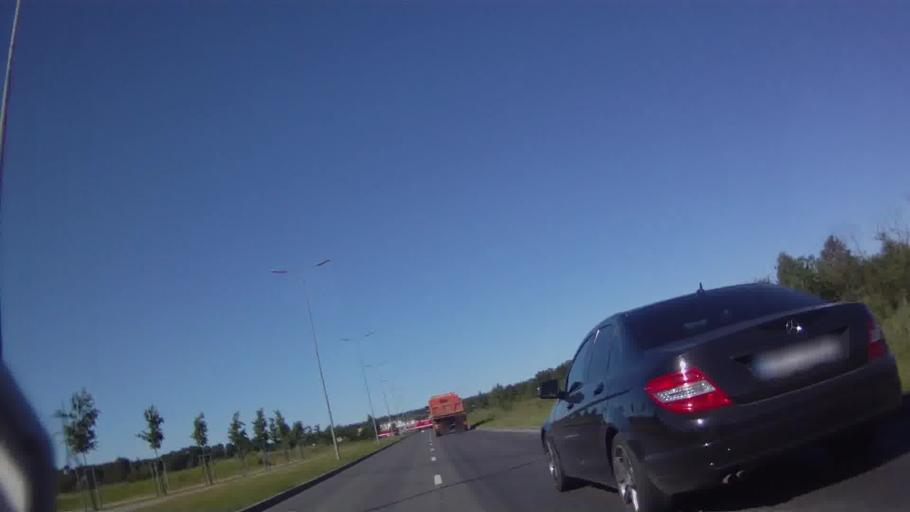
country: LV
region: Stopini
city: Ulbroka
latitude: 56.9520
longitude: 24.2500
